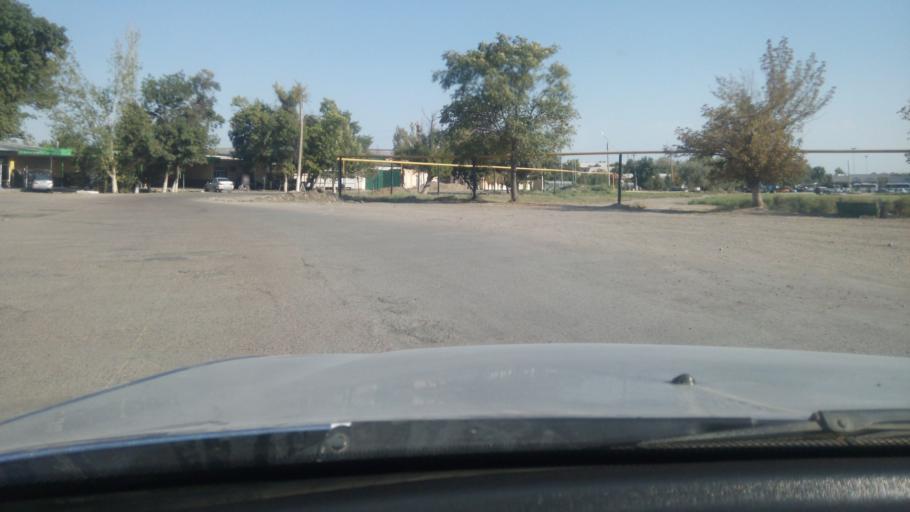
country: UZ
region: Sirdaryo
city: Guliston
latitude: 40.4998
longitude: 68.7643
